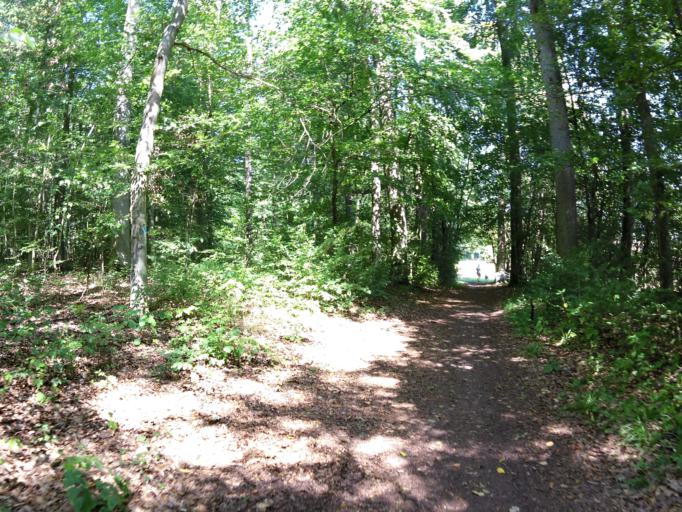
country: DE
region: Bavaria
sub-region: Regierungsbezirk Unterfranken
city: Gadheim
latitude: 49.8485
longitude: 9.8961
